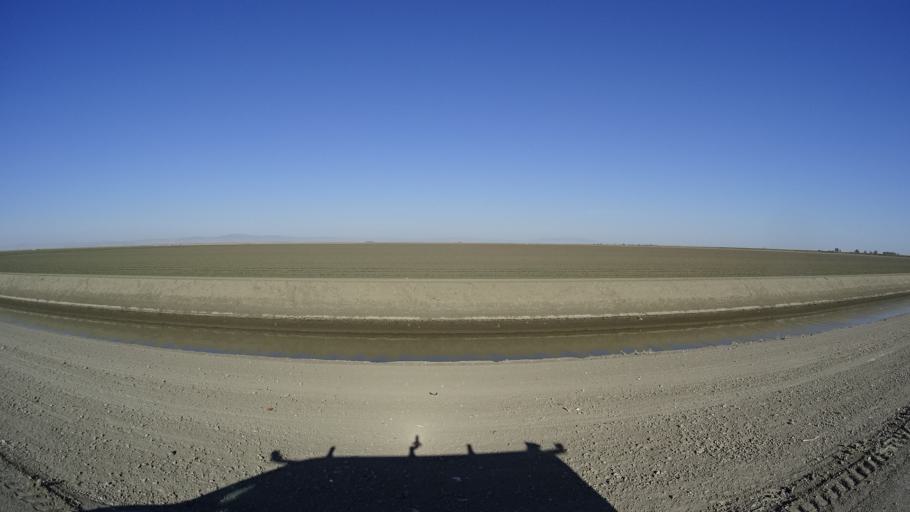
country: US
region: California
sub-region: Kings County
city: Stratford
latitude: 36.1321
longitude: -119.7984
